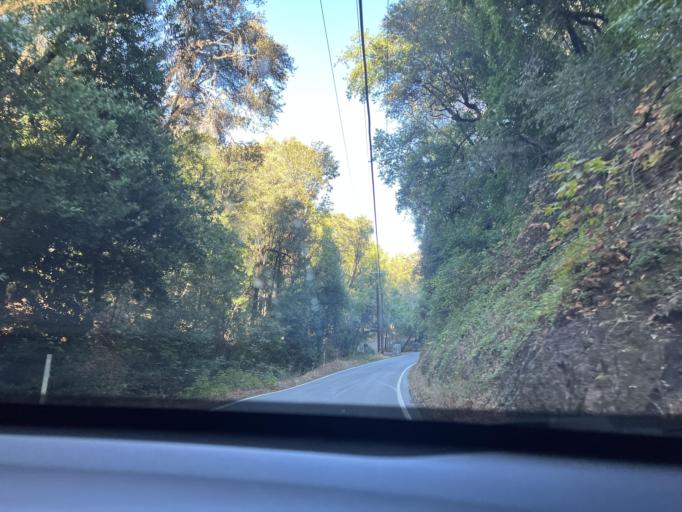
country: US
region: California
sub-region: Santa Clara County
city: Loyola
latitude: 37.2970
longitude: -122.1079
